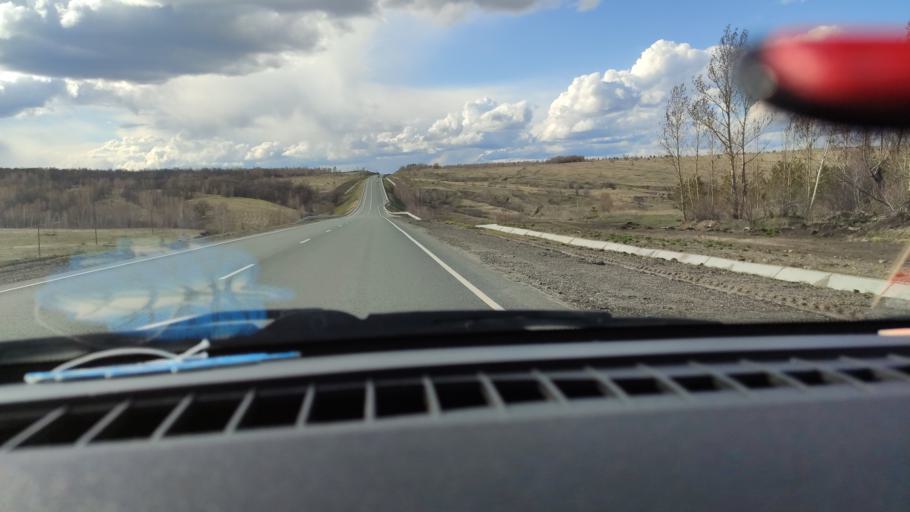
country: RU
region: Saratov
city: Shikhany
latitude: 52.1400
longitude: 47.2097
